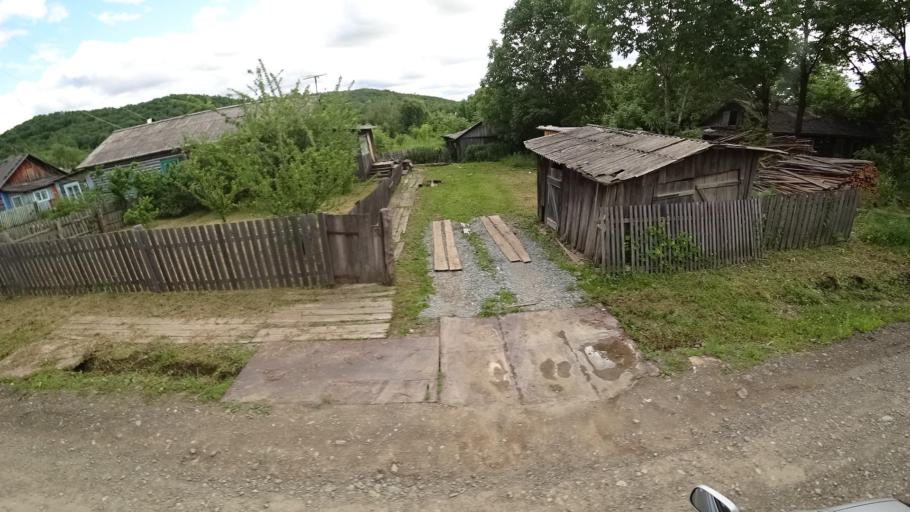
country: RU
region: Khabarovsk Krai
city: Litovko
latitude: 49.3662
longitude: 135.1764
